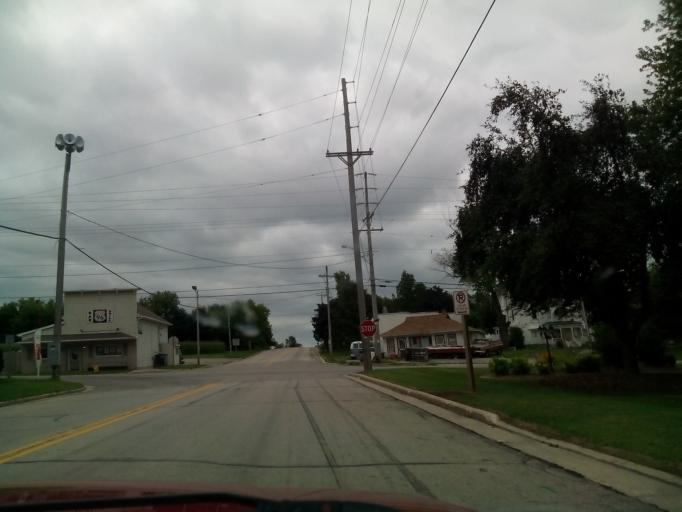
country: US
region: Wisconsin
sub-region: Outagamie County
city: Hortonville
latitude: 44.2730
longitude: -88.6377
